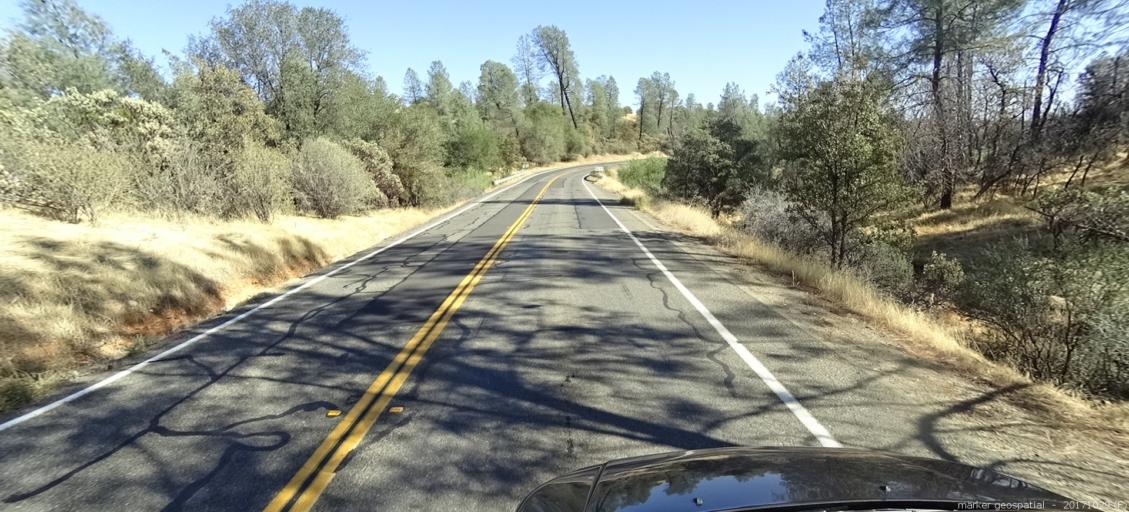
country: US
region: California
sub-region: Shasta County
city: Shasta
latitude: 40.4907
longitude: -122.5298
